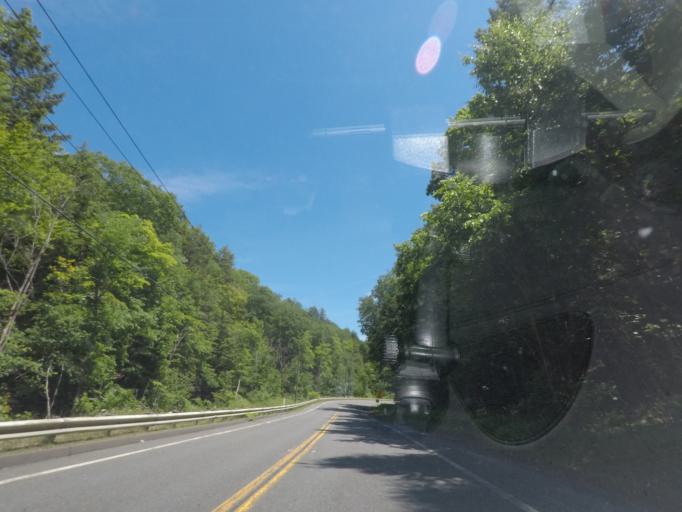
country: US
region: Massachusetts
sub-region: Berkshire County
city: Becket
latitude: 42.2686
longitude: -73.0152
